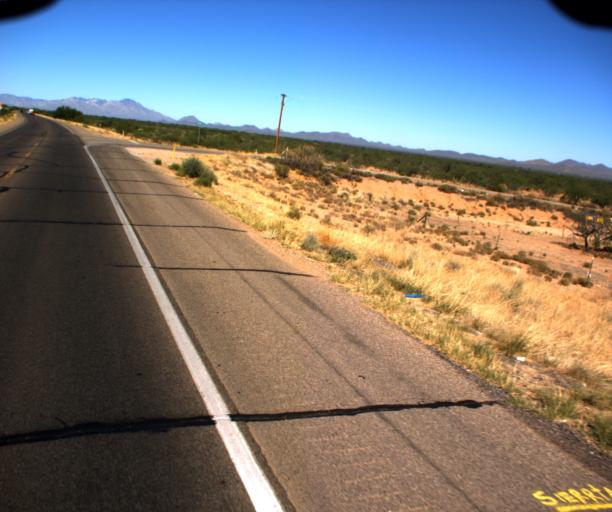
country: US
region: Arizona
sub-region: Pima County
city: Valencia West
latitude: 32.1235
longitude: -111.1996
